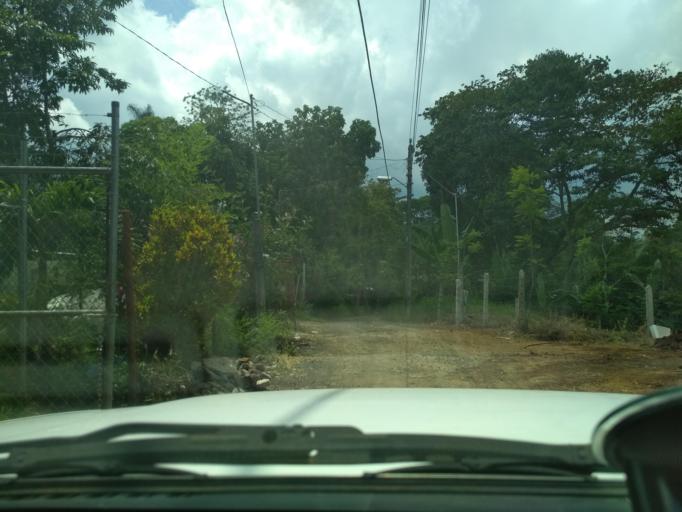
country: MX
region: Veracruz
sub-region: Cordoba
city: San Jose de Abajo [Unidad Habitacional]
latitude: 18.9192
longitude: -96.9577
